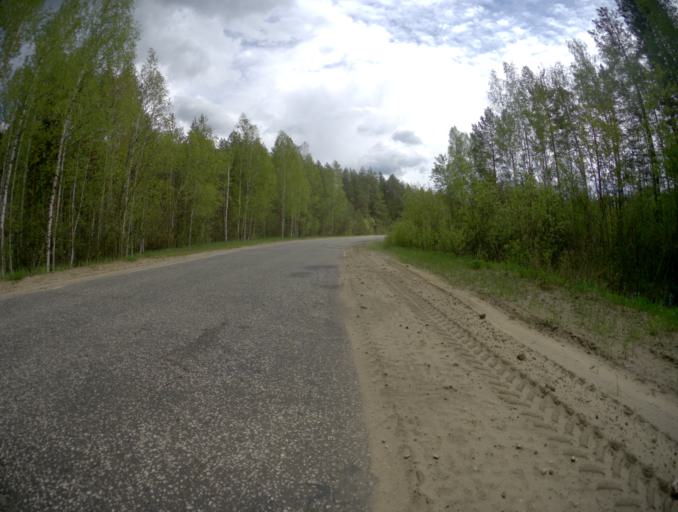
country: RU
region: Vladimir
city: Velikodvorskiy
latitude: 55.3964
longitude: 40.7022
